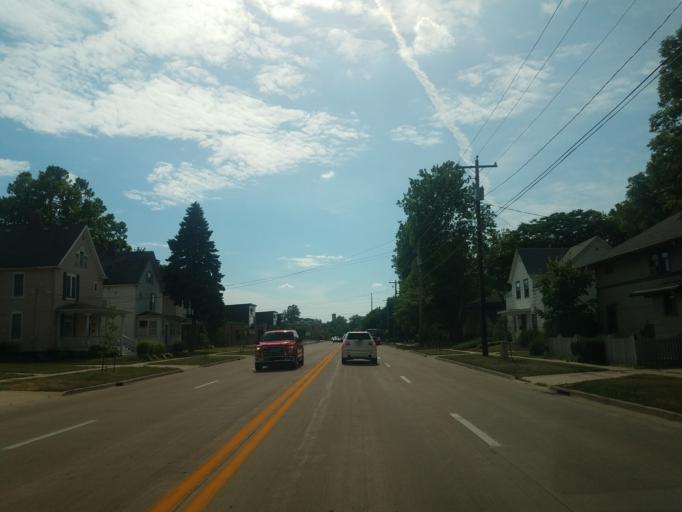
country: US
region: Illinois
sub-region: McLean County
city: Bloomington
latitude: 40.4799
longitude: -88.9791
